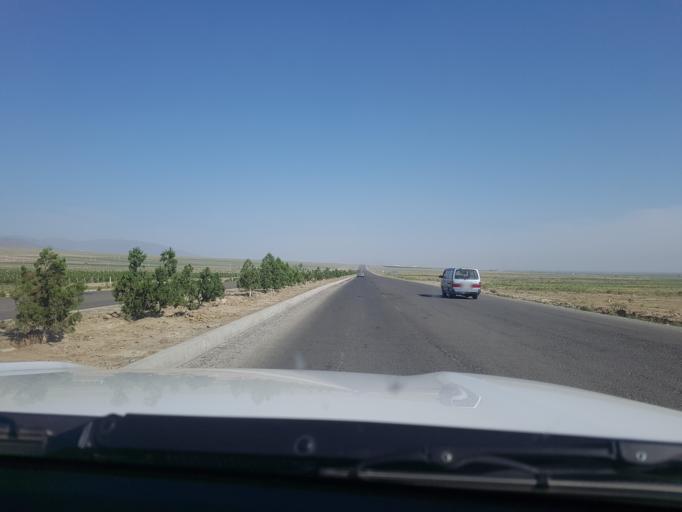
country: TM
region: Ahal
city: Baharly
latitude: 38.4489
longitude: 57.3740
